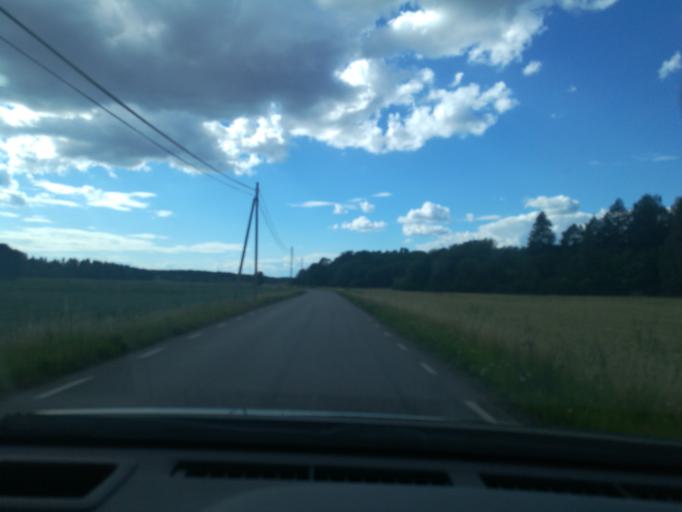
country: SE
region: Soedermanland
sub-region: Eskilstuna Kommun
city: Arla
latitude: 59.4487
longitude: 16.7456
